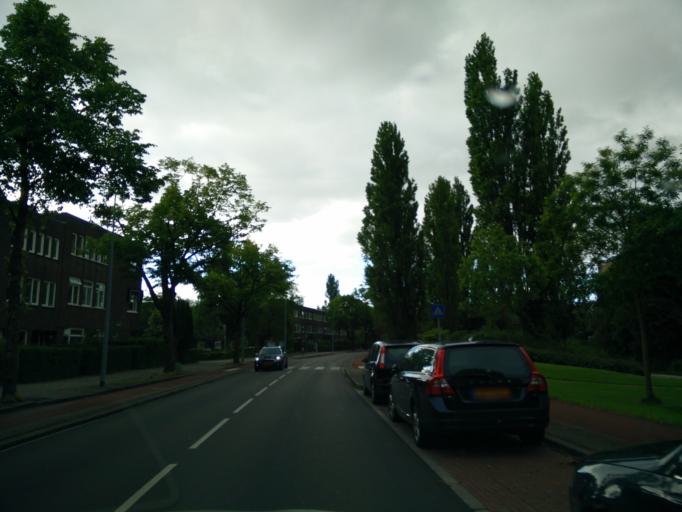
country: NL
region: Groningen
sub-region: Gemeente Groningen
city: Oosterpark
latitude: 53.2242
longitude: 6.5765
